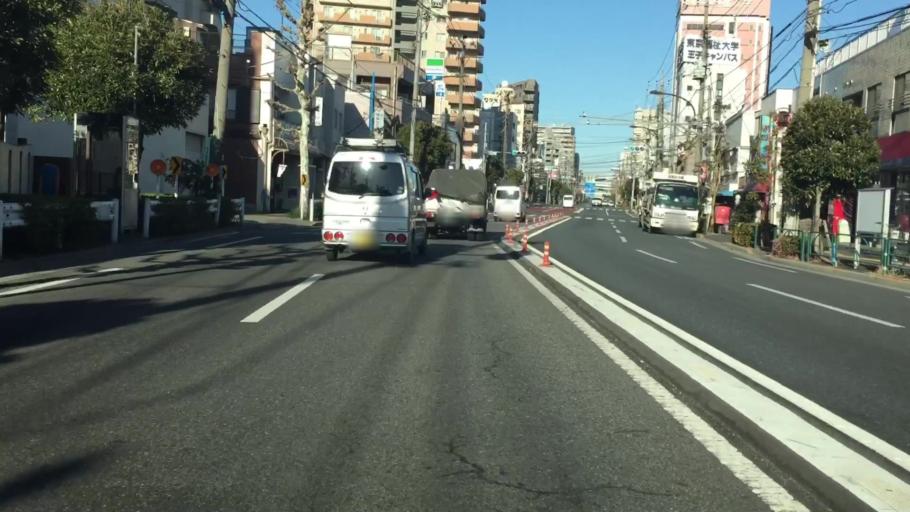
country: JP
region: Saitama
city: Kawaguchi
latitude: 35.7502
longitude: 139.7491
